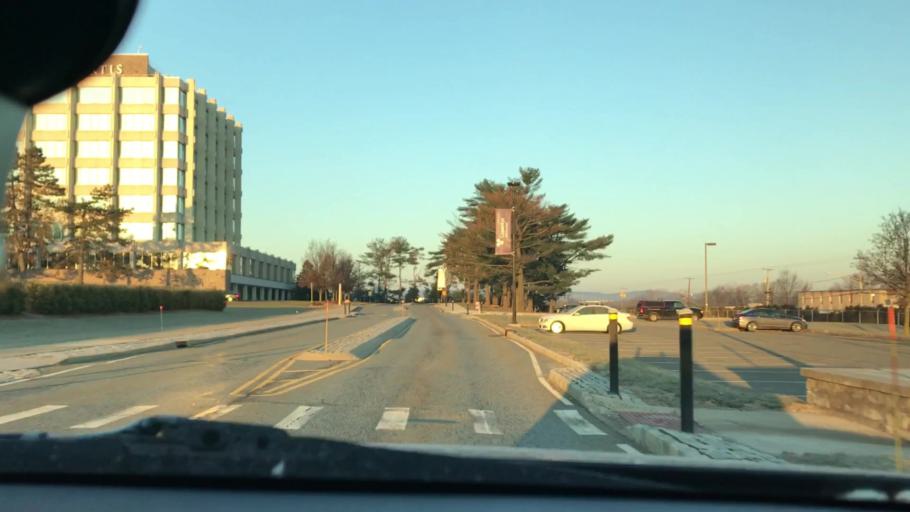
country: US
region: New Jersey
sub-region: Morris County
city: Hanover
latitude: 40.8114
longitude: -74.3886
